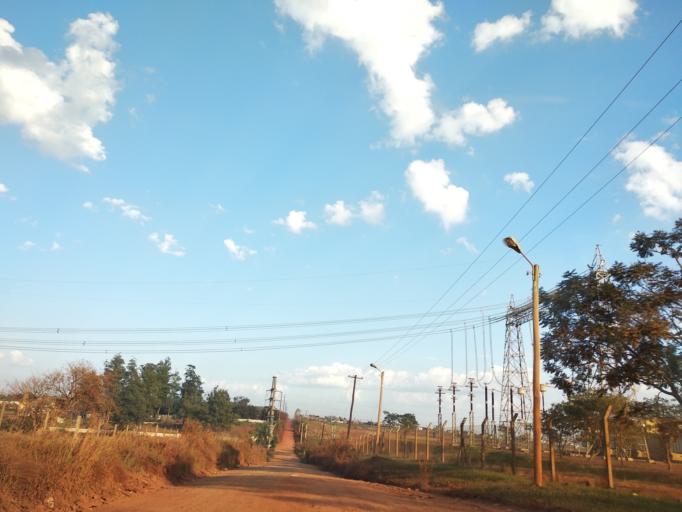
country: AR
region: Misiones
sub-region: Departamento de Capital
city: Posadas
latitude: -27.4448
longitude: -55.9179
